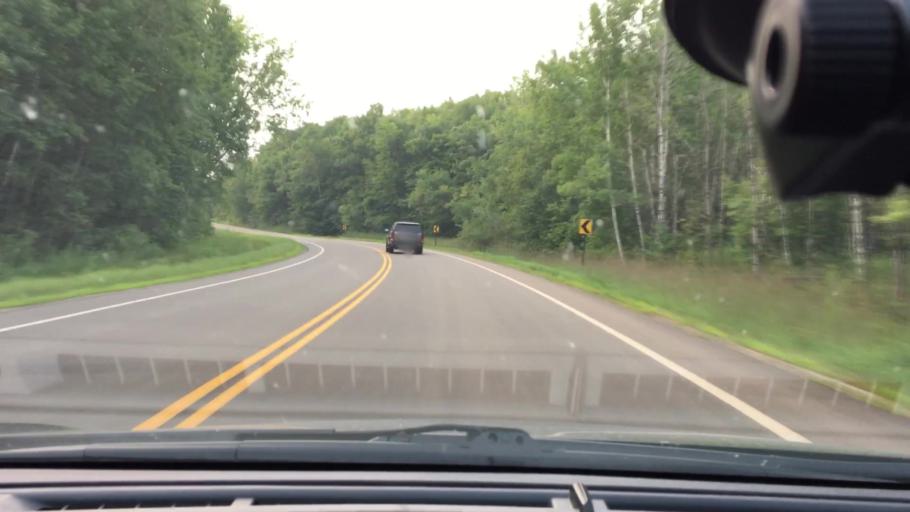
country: US
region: Minnesota
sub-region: Crow Wing County
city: Crosby
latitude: 46.5228
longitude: -93.9246
